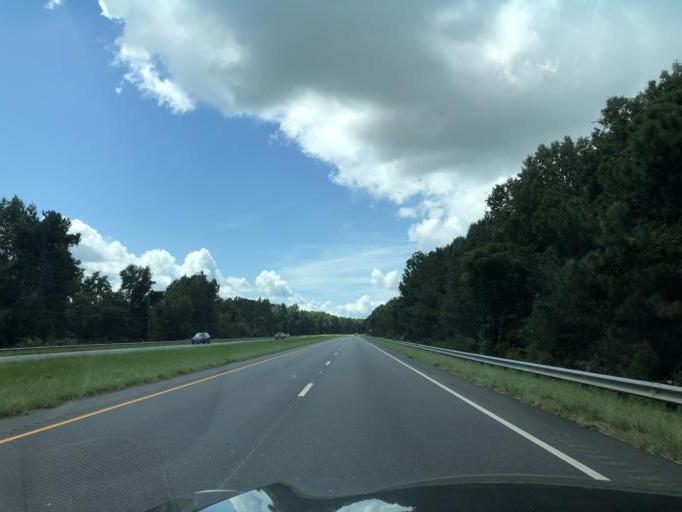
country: US
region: Alabama
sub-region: Barbour County
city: Eufaula
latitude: 31.9745
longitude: -85.1151
